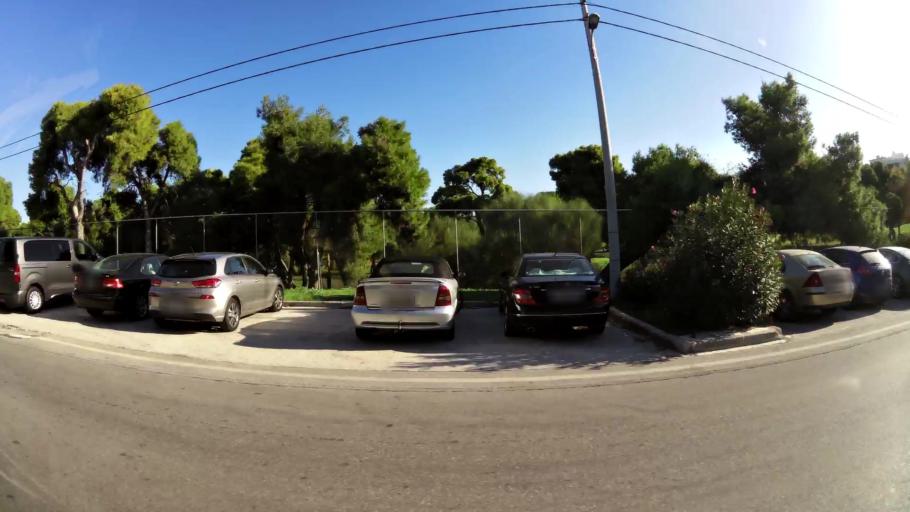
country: GR
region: Attica
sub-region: Nomarchia Athinas
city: Glyfada
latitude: 37.8680
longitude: 23.7440
